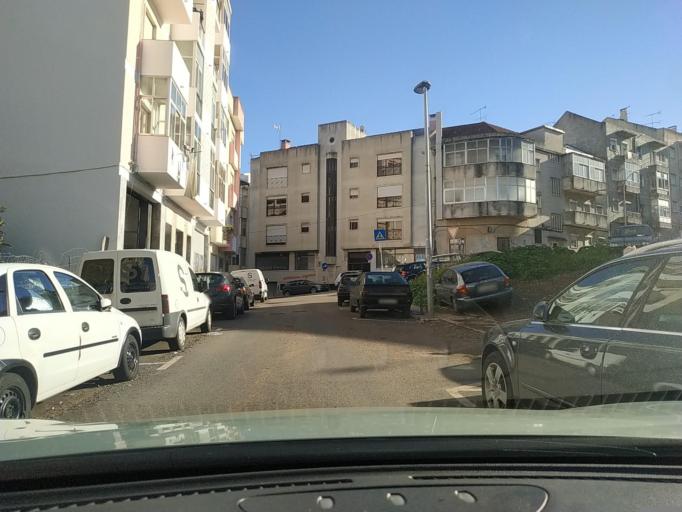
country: PT
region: Lisbon
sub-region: Odivelas
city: Pontinha
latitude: 38.7684
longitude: -9.2154
